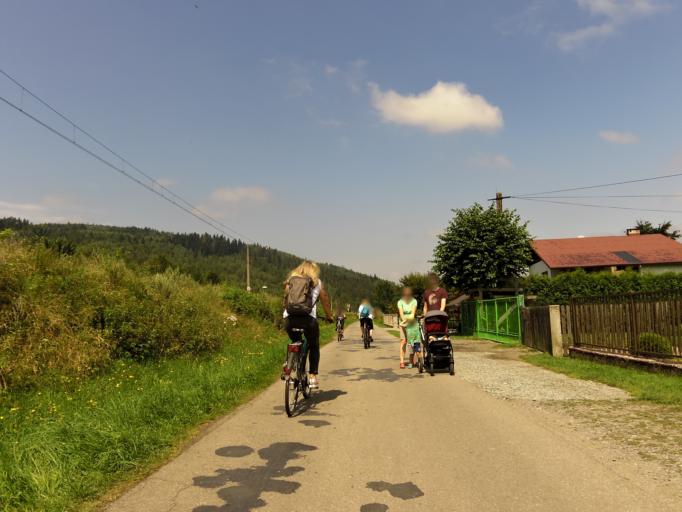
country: PL
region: Silesian Voivodeship
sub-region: Powiat zywiecki
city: Rajcza
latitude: 49.5208
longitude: 19.1095
